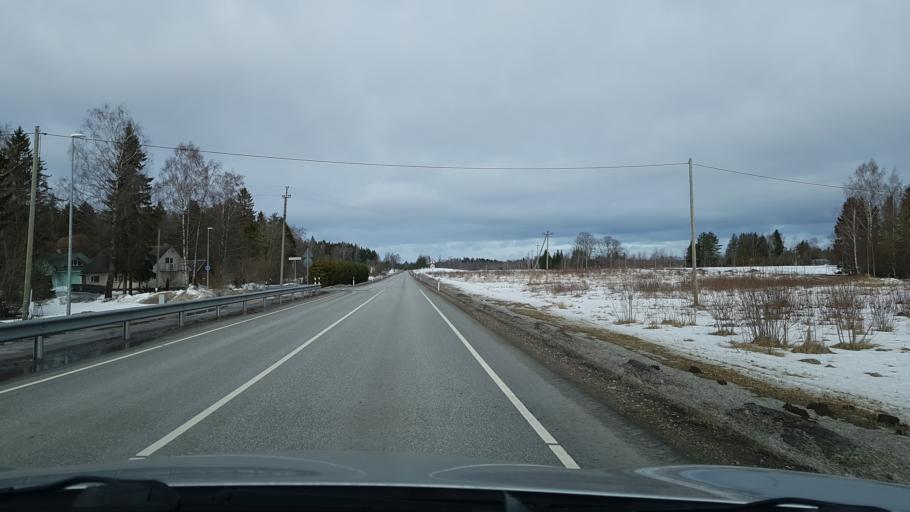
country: EE
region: Jogevamaa
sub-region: Jogeva linn
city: Jogeva
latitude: 58.7628
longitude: 26.3330
